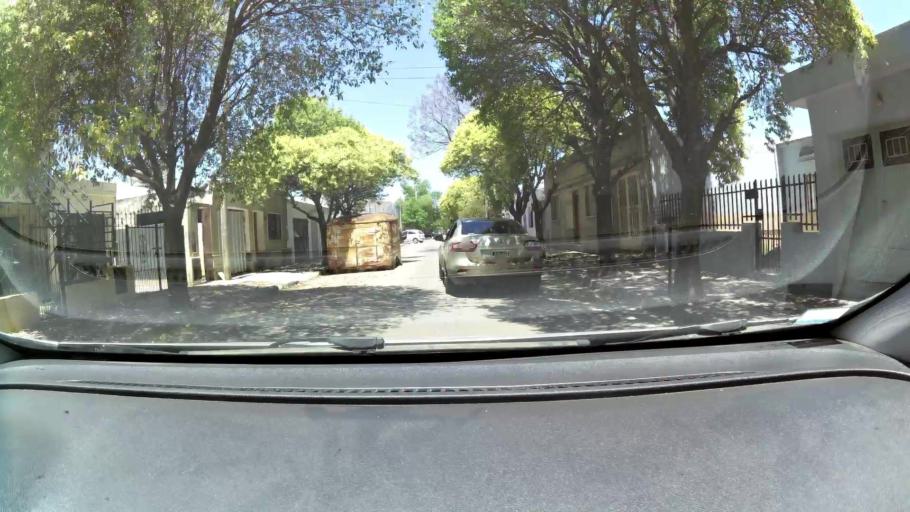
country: AR
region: Cordoba
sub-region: Departamento de Capital
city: Cordoba
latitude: -31.3817
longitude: -64.1356
